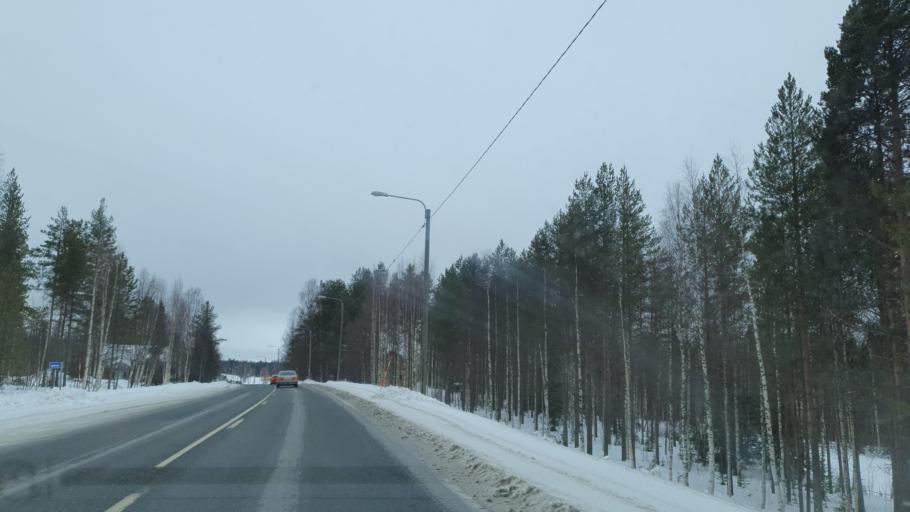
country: SE
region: Norrbotten
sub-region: Overtornea Kommun
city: OEvertornea
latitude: 66.4983
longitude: 23.7515
